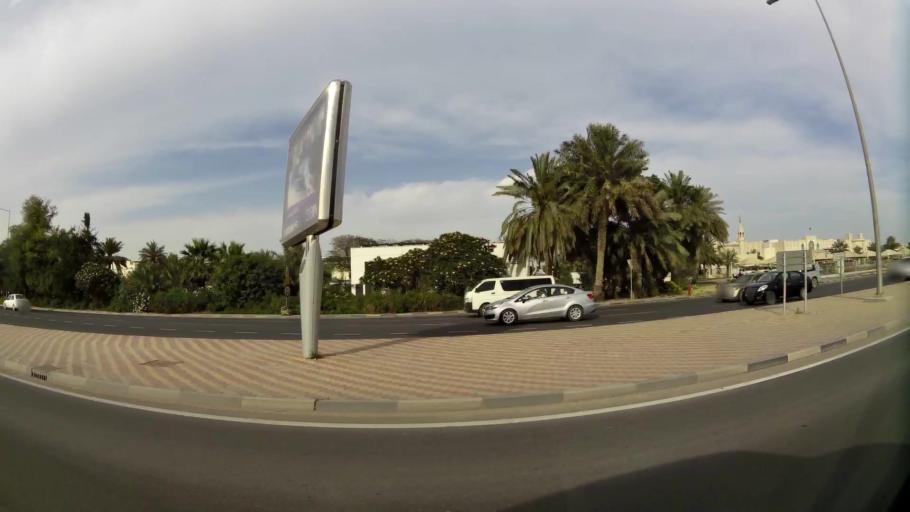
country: QA
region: Baladiyat ad Dawhah
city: Doha
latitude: 25.2515
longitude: 51.5369
